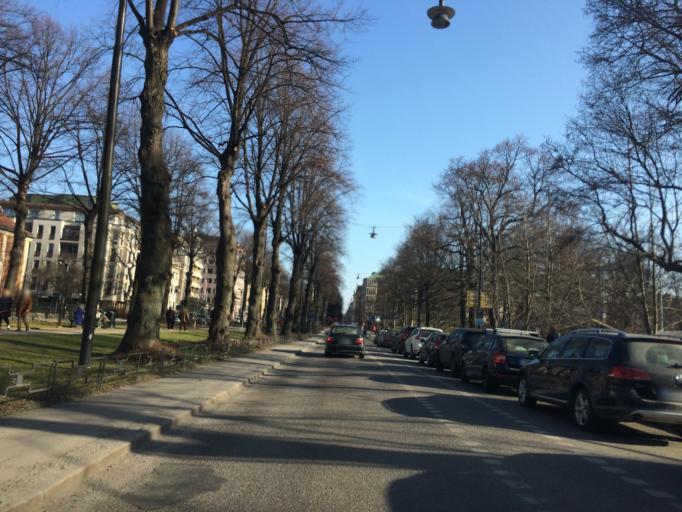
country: SE
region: Stockholm
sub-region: Stockholms Kommun
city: Stockholm
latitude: 59.3411
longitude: 18.0728
